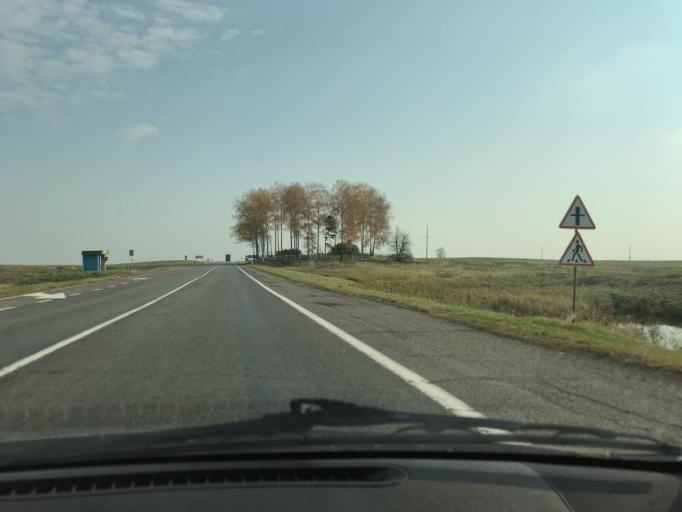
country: BY
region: Vitebsk
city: Chashniki
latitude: 55.0132
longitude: 29.0596
